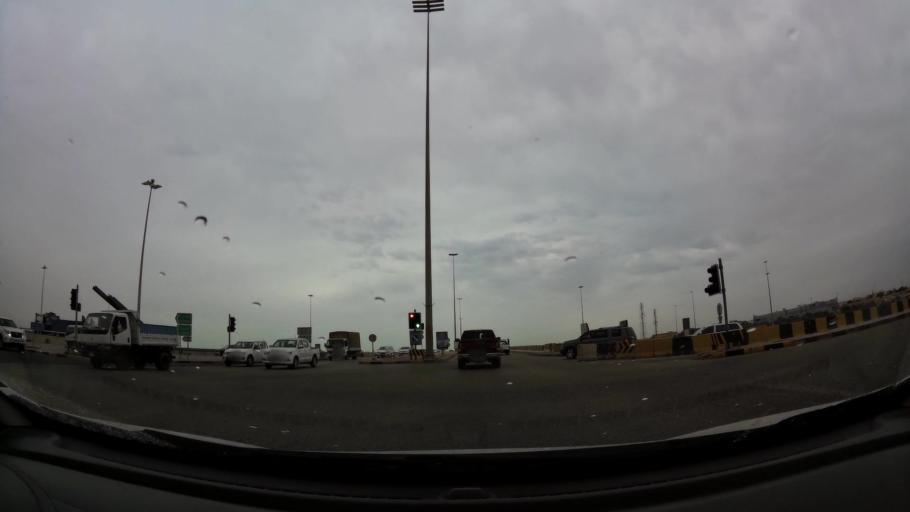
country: BH
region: Central Governorate
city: Madinat Hamad
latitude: 26.1709
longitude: 50.4655
